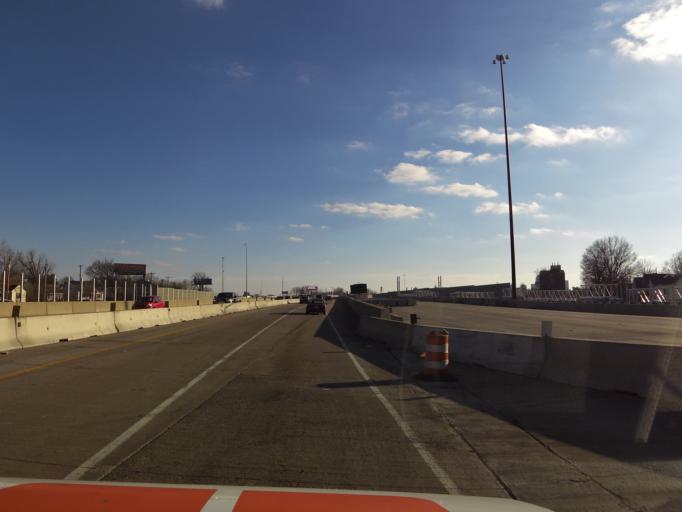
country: US
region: Indiana
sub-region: Clark County
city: Clarksville
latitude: 38.2869
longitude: -85.7560
